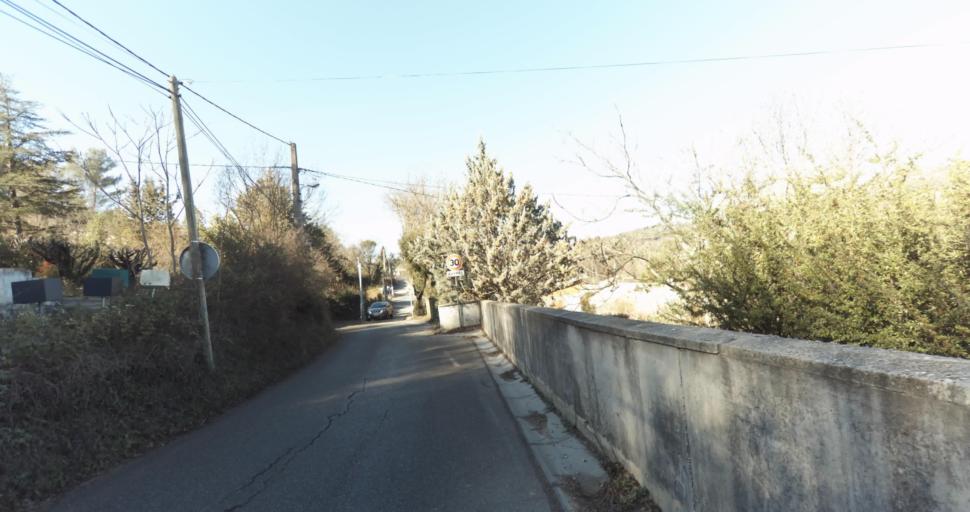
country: FR
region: Provence-Alpes-Cote d'Azur
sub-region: Departement des Bouches-du-Rhone
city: La Bouilladisse
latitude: 43.3907
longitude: 5.5897
